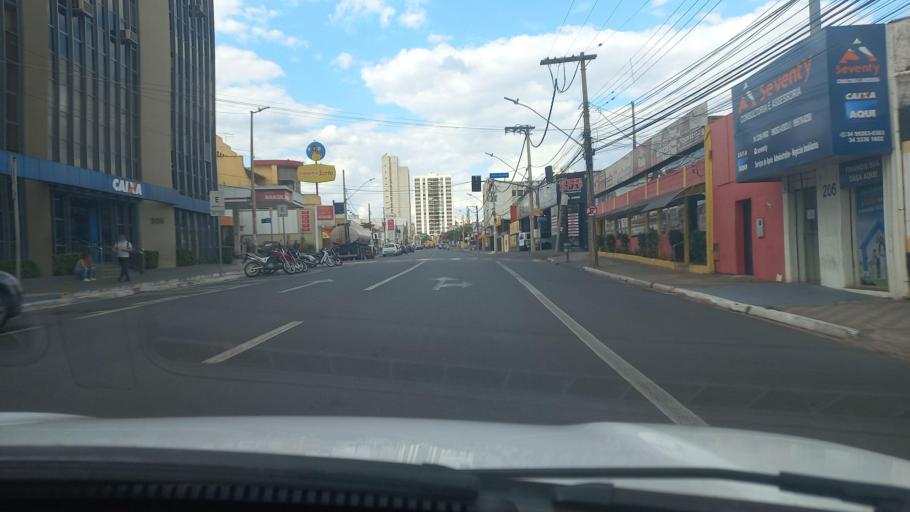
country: BR
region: Minas Gerais
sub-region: Uberaba
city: Uberaba
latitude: -19.7464
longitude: -47.9343
